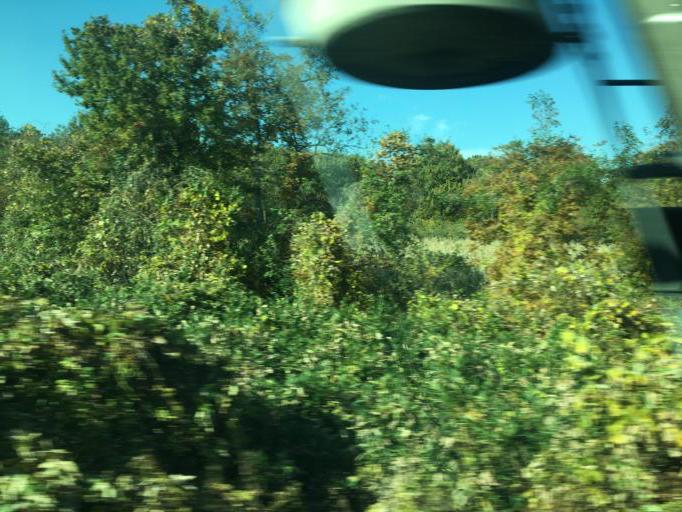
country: JP
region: Ibaraki
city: Iwase
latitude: 36.3380
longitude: 140.0587
